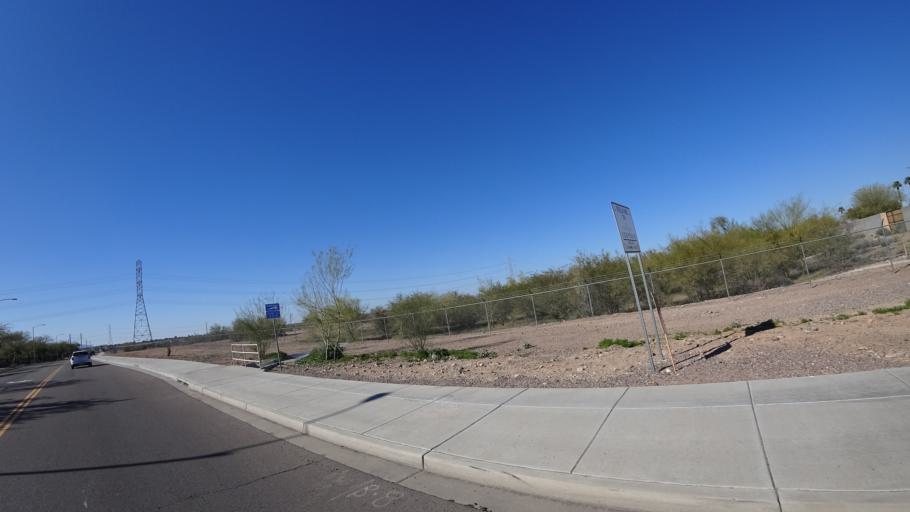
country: US
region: Arizona
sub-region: Maricopa County
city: Surprise
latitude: 33.6526
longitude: -112.2988
